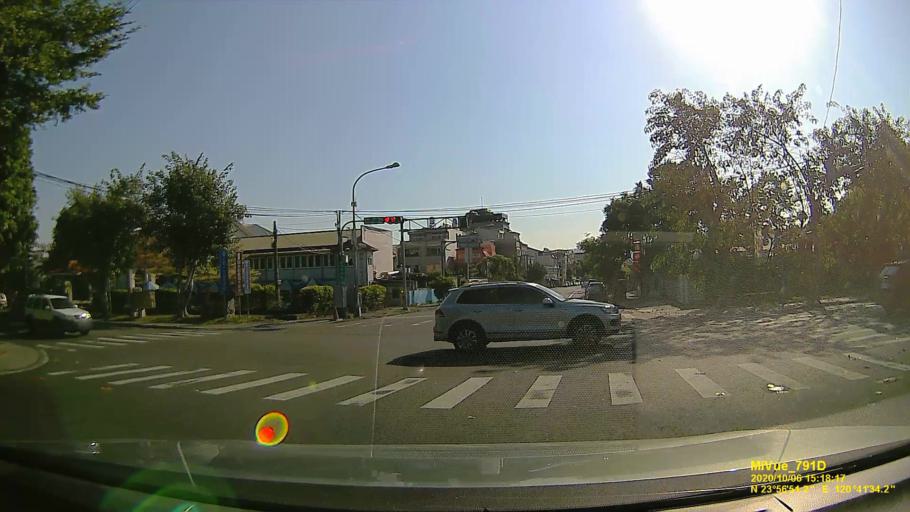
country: TW
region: Taiwan
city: Zhongxing New Village
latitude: 23.9476
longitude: 120.6928
